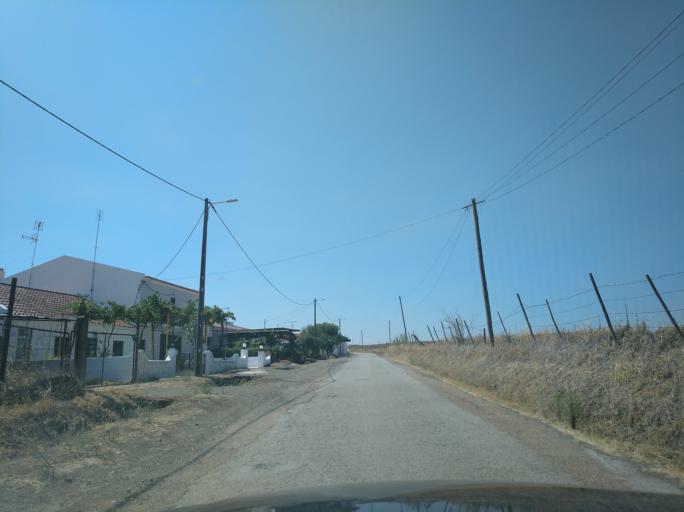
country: PT
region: Portalegre
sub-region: Campo Maior
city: Campo Maior
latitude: 39.0202
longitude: -7.0791
